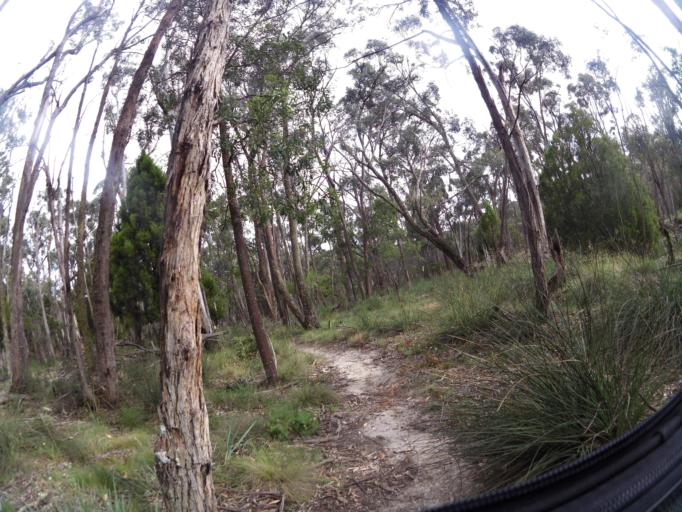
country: AU
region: Victoria
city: Brown Hill
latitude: -37.4714
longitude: 143.9096
